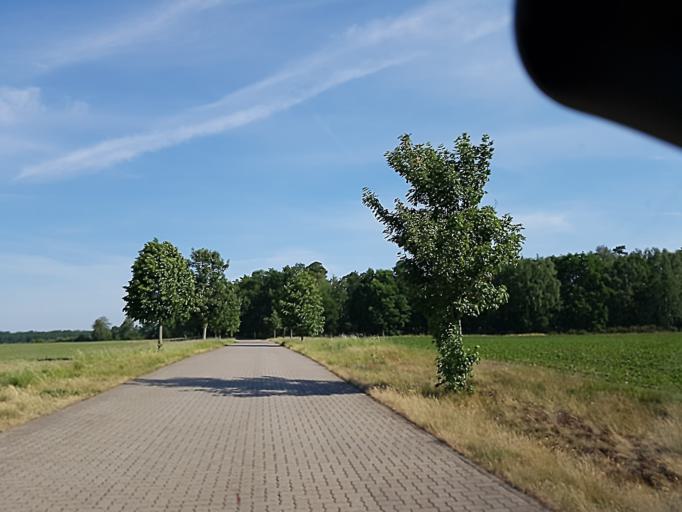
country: DE
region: Brandenburg
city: Gorzke
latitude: 52.0396
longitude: 12.2784
